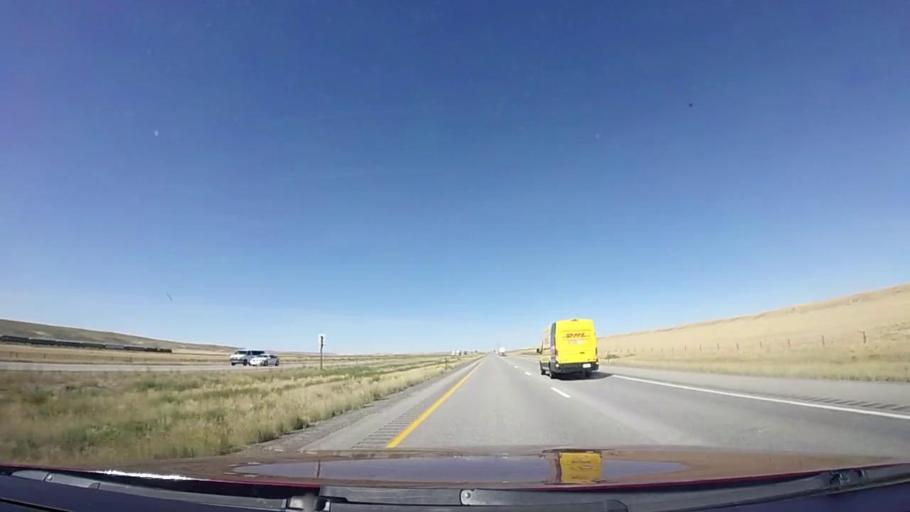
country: US
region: Wyoming
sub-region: Carbon County
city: Rawlins
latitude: 41.6573
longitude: -108.0930
